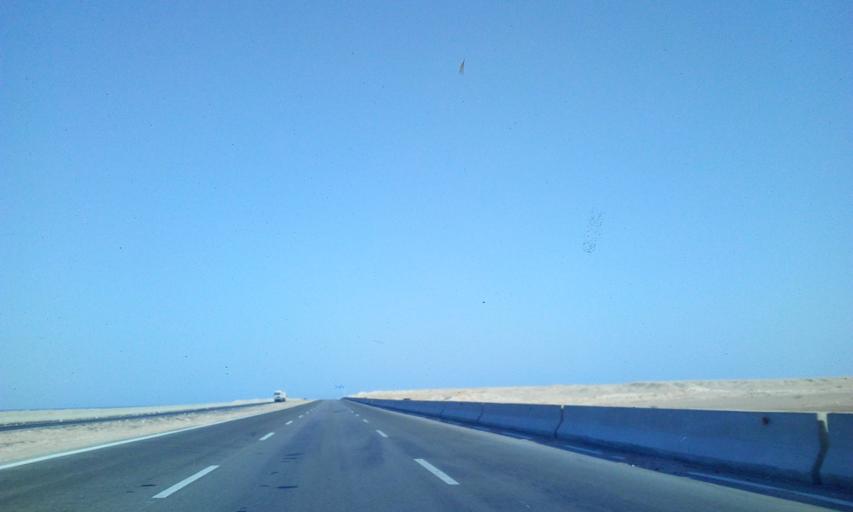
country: EG
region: As Suways
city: Ain Sukhna
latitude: 29.0994
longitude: 32.6228
